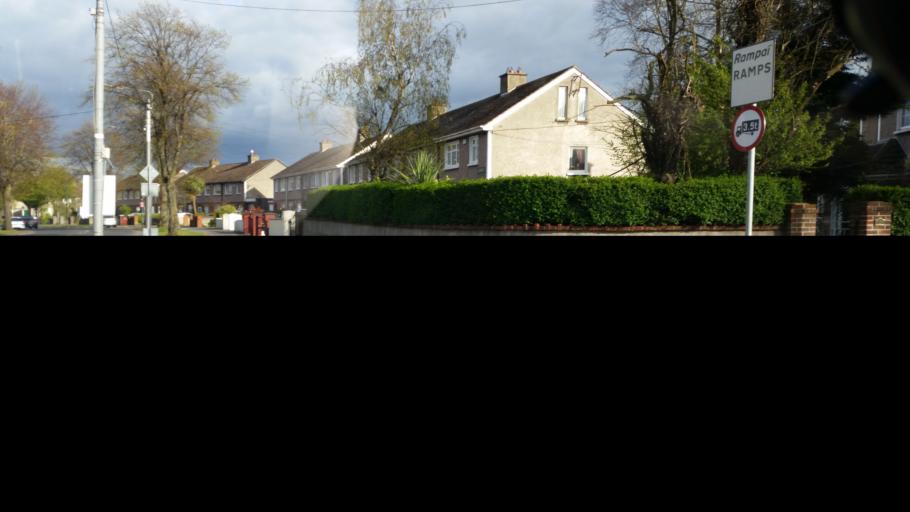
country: IE
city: Coolock
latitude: 53.3827
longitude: -6.2046
